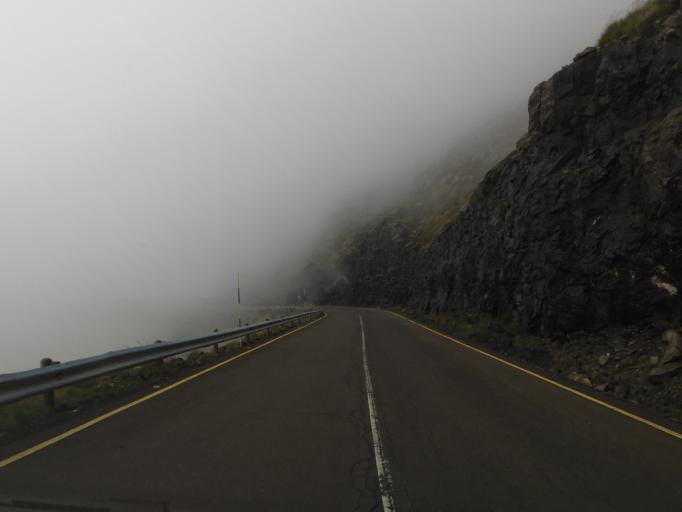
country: LS
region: Butha-Buthe
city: Butha-Buthe
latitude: -29.0612
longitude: 28.4022
